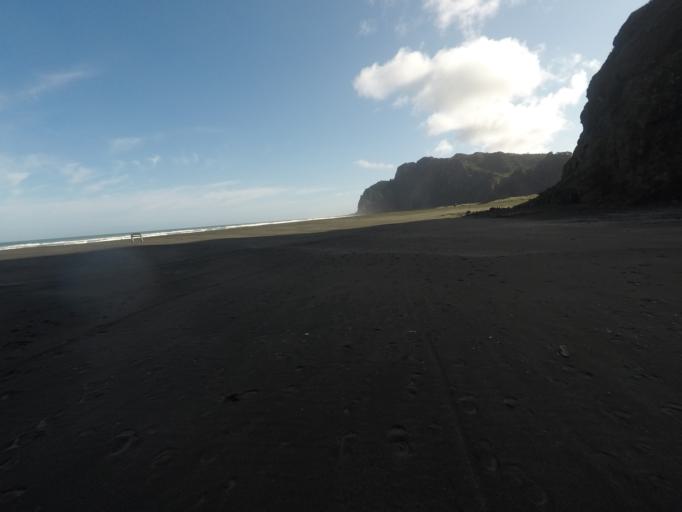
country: NZ
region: Auckland
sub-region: Auckland
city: Muriwai Beach
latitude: -36.9943
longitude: 174.4735
